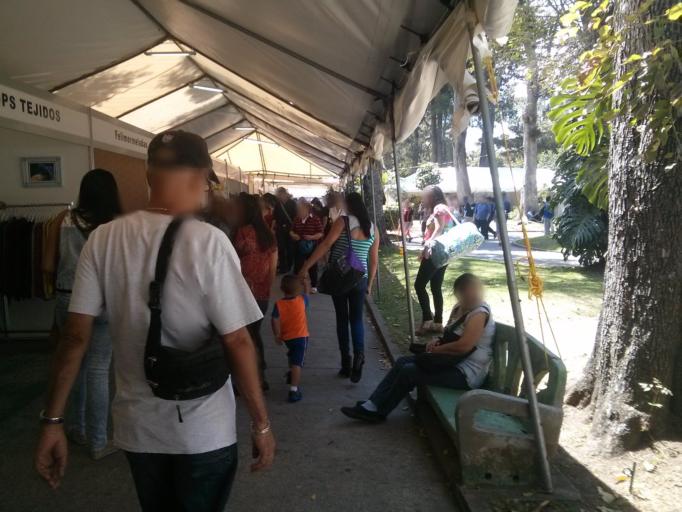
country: CR
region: San Jose
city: San Jose
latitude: 9.9344
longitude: -84.0703
